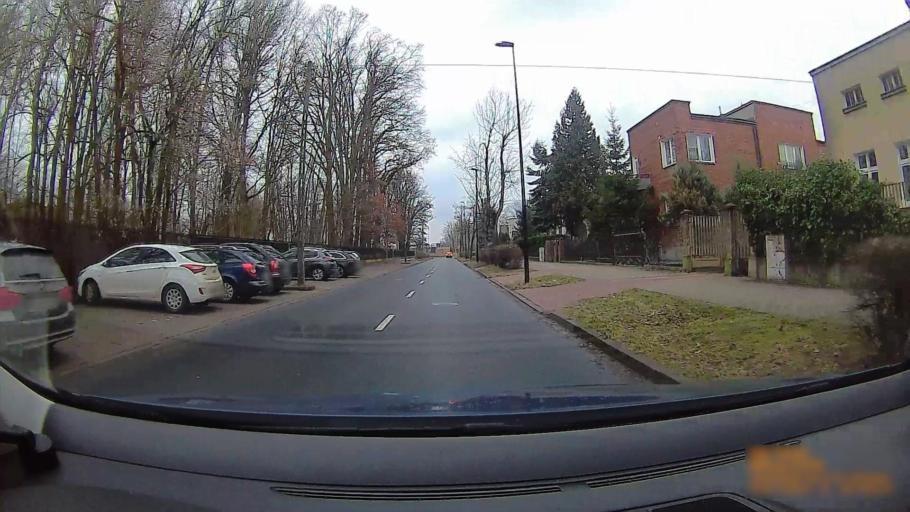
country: PL
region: Greater Poland Voivodeship
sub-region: Konin
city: Konin
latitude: 52.2110
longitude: 18.2464
